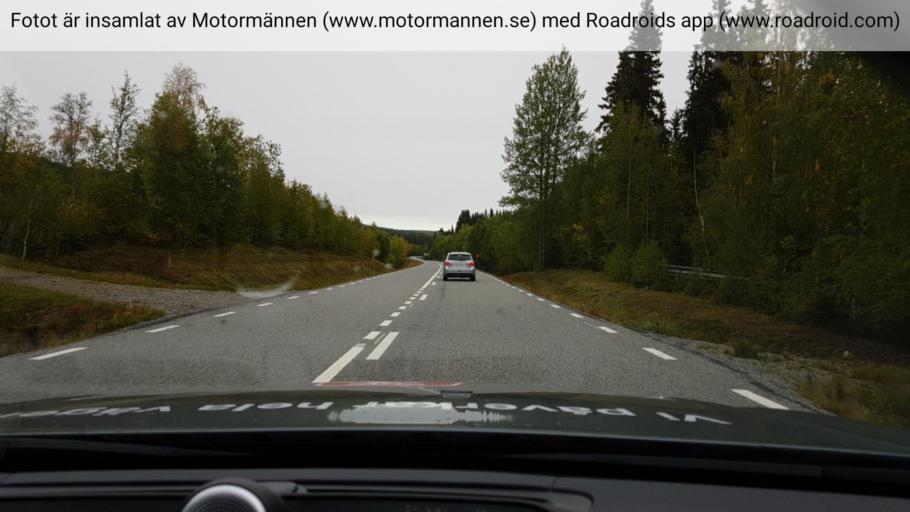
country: SE
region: Jaemtland
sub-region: Stroemsunds Kommun
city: Stroemsund
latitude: 64.0600
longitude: 15.5519
